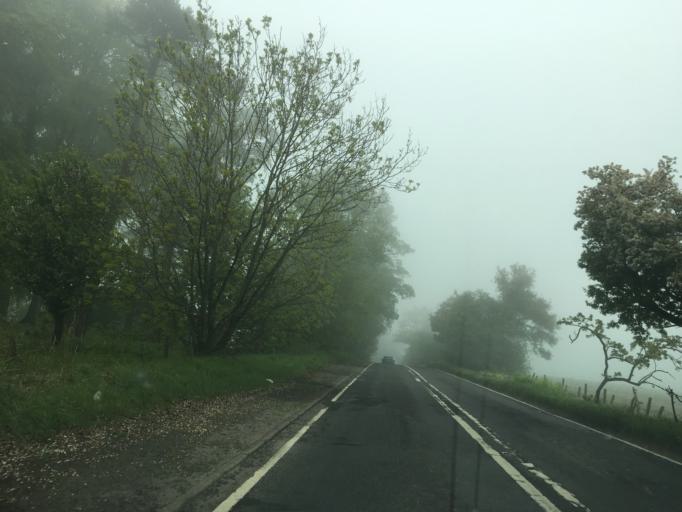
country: GB
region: Scotland
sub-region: Midlothian
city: Penicuik
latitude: 55.8199
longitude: -3.2022
